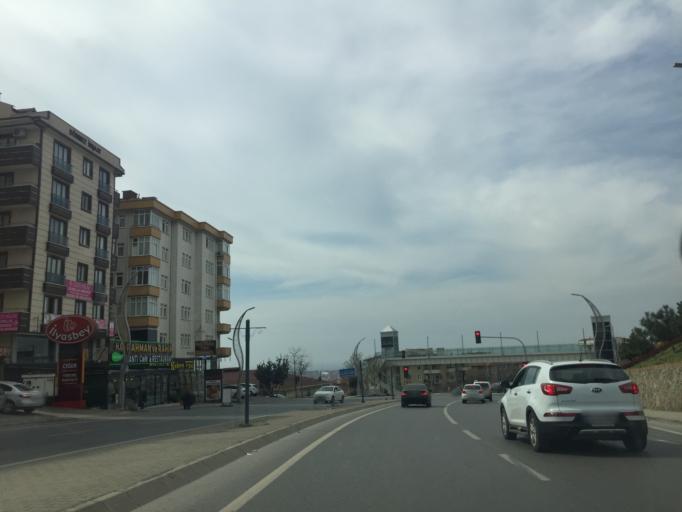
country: TR
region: Kocaeli
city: Gebze
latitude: 40.7890
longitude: 29.4182
